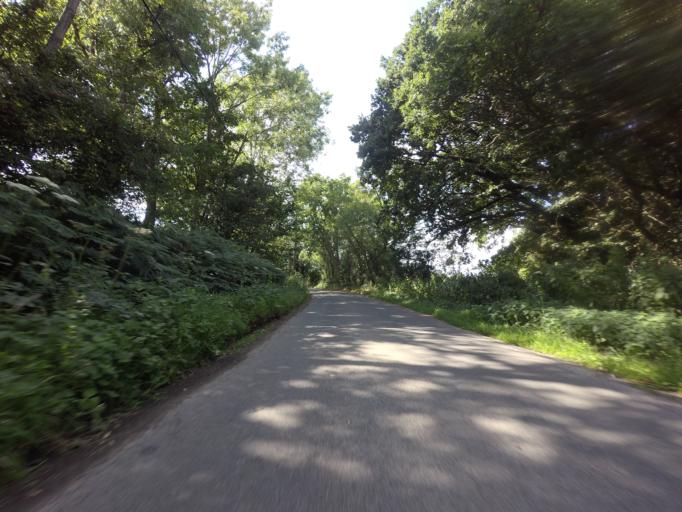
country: GB
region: England
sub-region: East Sussex
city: Rye
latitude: 50.9825
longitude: 0.7370
